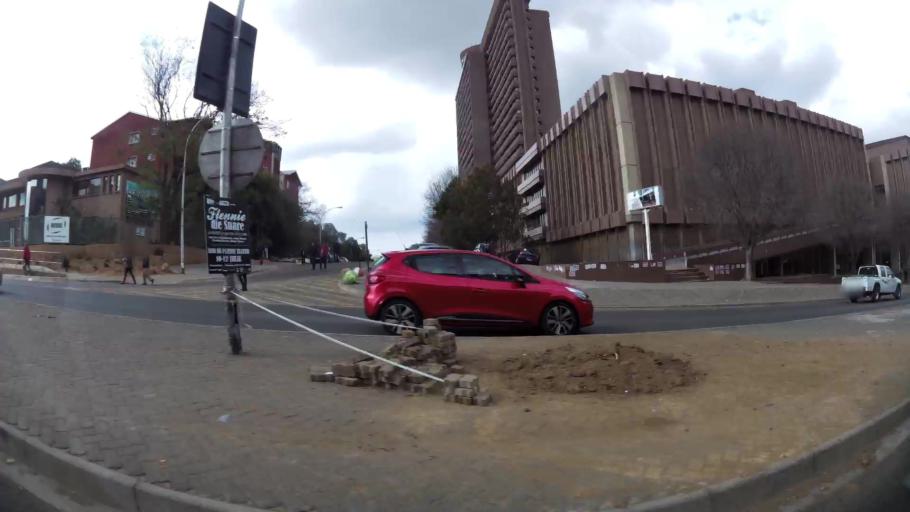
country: ZA
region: Orange Free State
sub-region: Mangaung Metropolitan Municipality
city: Bloemfontein
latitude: -29.1150
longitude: 26.2117
